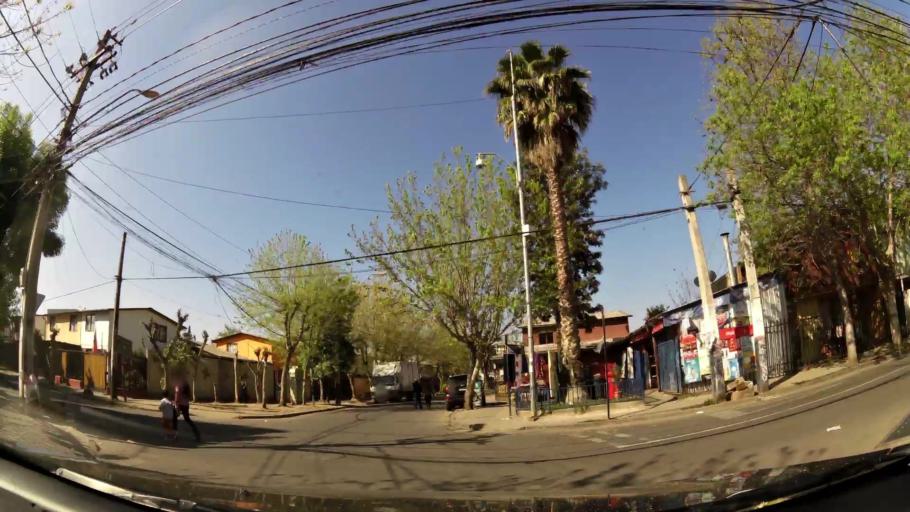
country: CL
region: Santiago Metropolitan
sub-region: Provincia de Chacabuco
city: Chicureo Abajo
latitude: -33.3575
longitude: -70.6894
